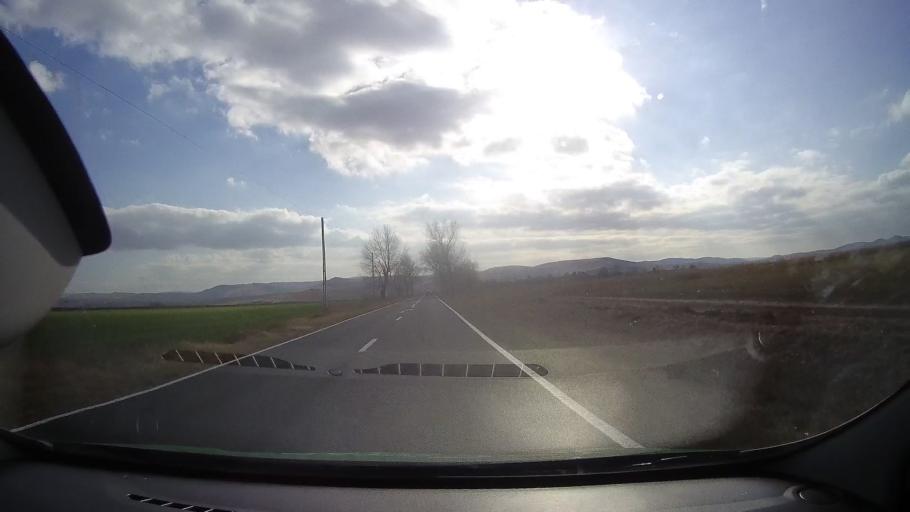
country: RO
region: Tulcea
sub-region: Comuna Nalbant
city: Nicolae Balcescu
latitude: 45.0057
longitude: 28.5975
